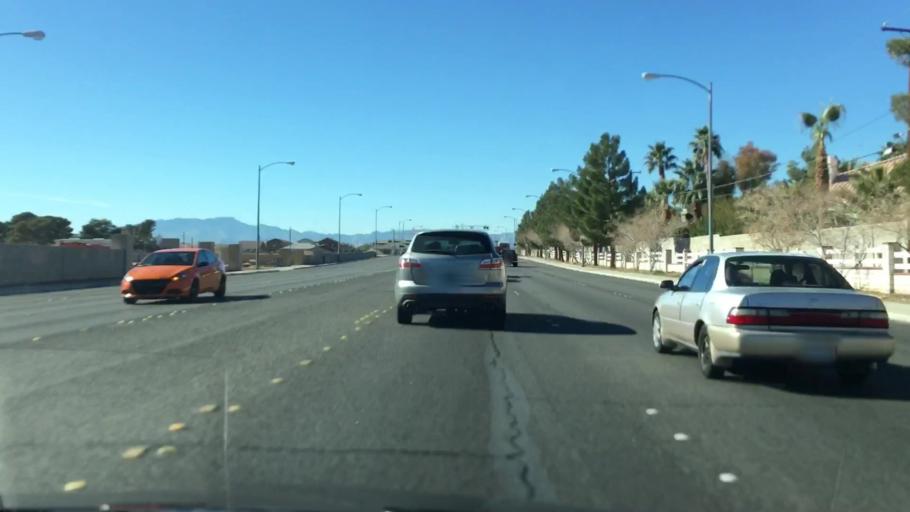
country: US
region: Nevada
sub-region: Clark County
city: Whitney
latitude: 36.0570
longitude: -115.1095
